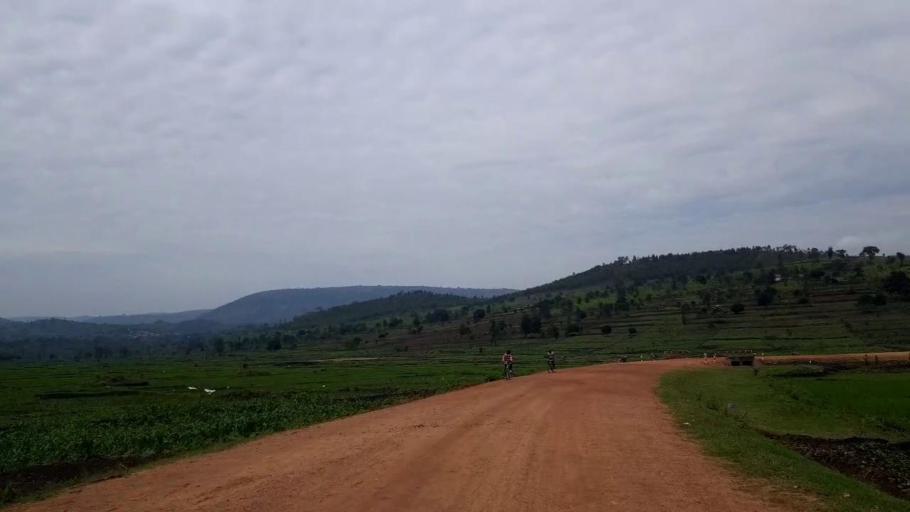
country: RW
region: Northern Province
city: Byumba
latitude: -1.5008
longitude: 30.2309
